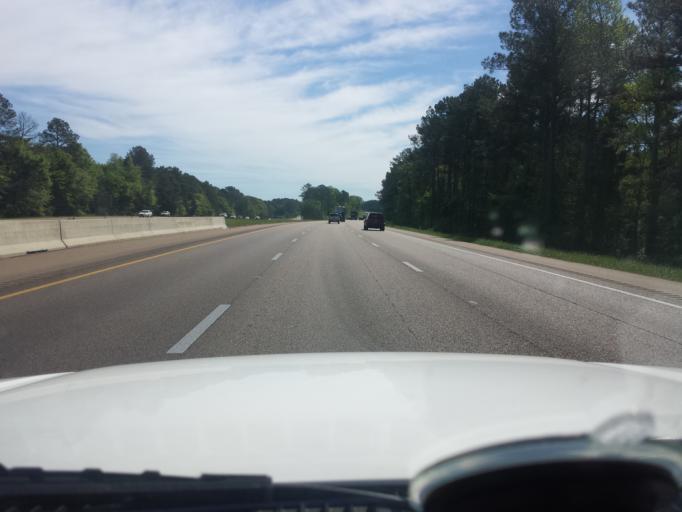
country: US
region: Mississippi
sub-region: Rankin County
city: Pearl
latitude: 32.2664
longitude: -90.1188
